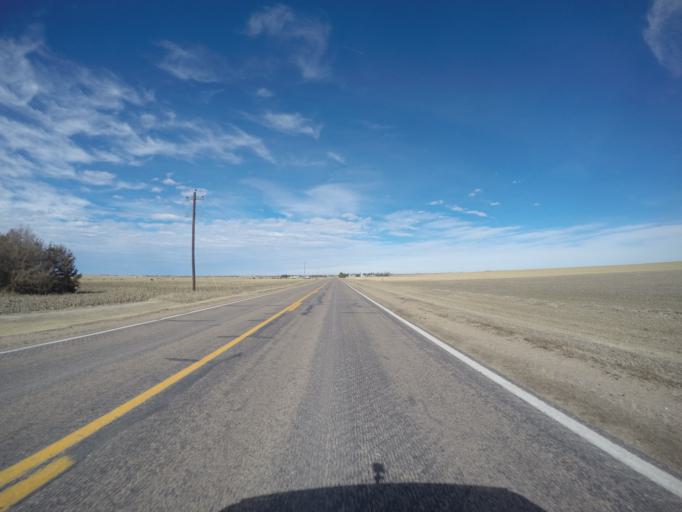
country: US
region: Nebraska
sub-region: Franklin County
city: Franklin
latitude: 40.1676
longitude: -98.9527
